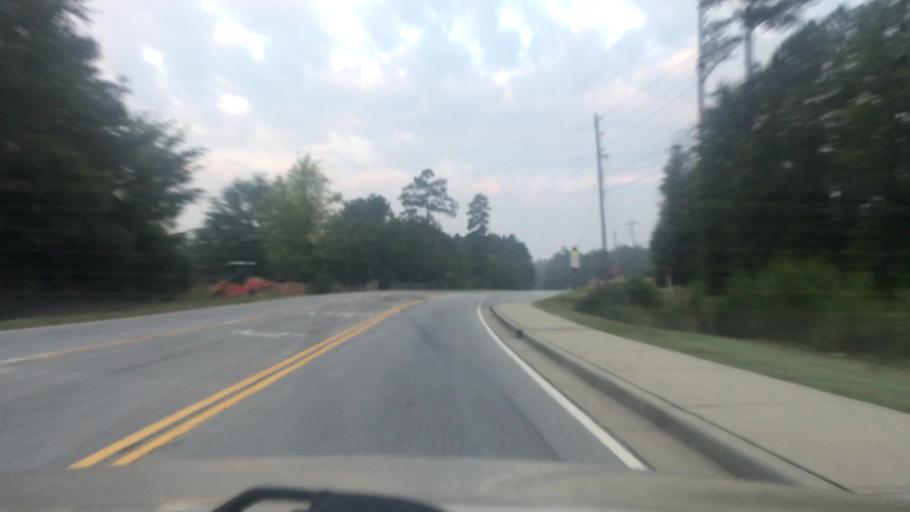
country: US
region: South Carolina
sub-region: Lexington County
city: Irmo
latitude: 34.1512
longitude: -81.2021
